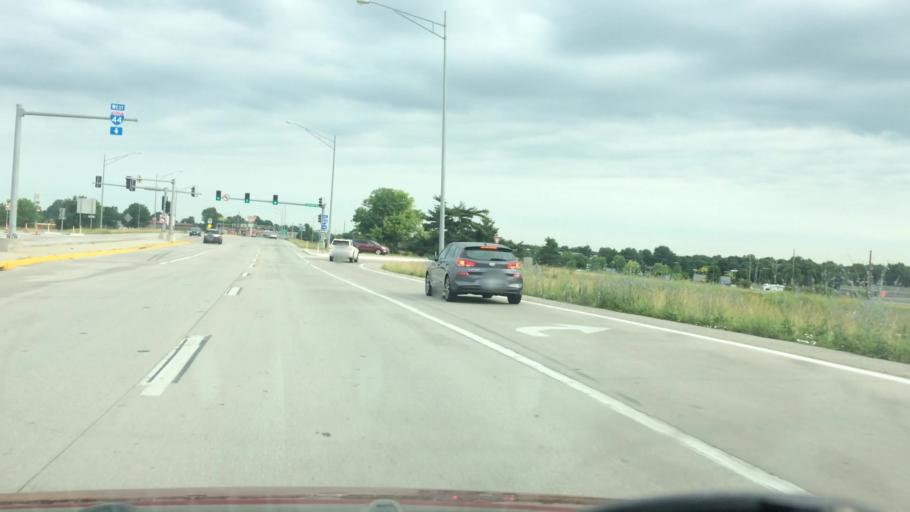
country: US
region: Missouri
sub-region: Greene County
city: Springfield
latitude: 37.2481
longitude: -93.2611
